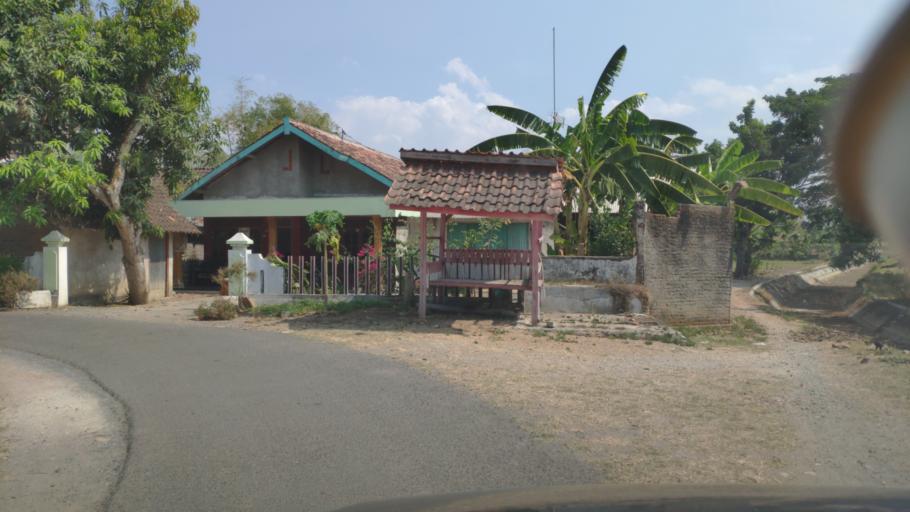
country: ID
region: Central Java
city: Tempuran
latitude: -6.9112
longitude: 111.4597
